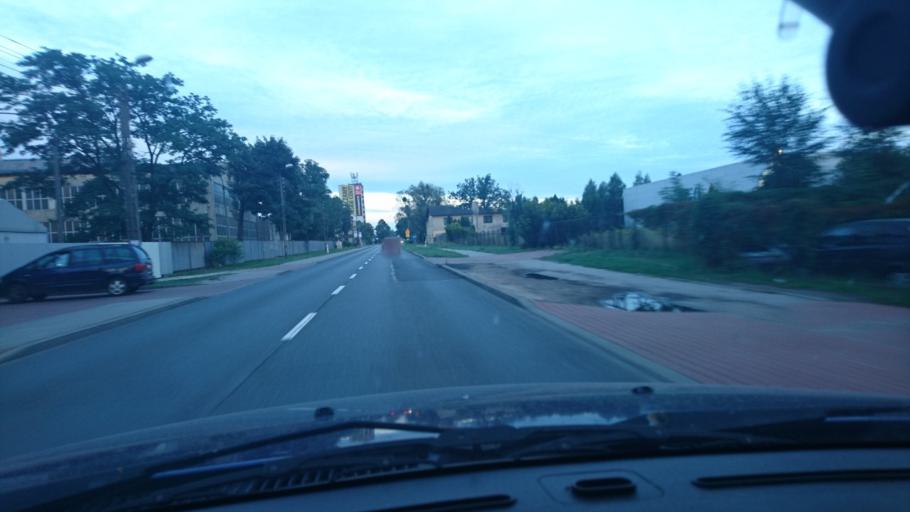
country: PL
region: Silesian Voivodeship
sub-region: Powiat tarnogorski
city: Zbroslawice
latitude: 50.4782
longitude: 18.7943
